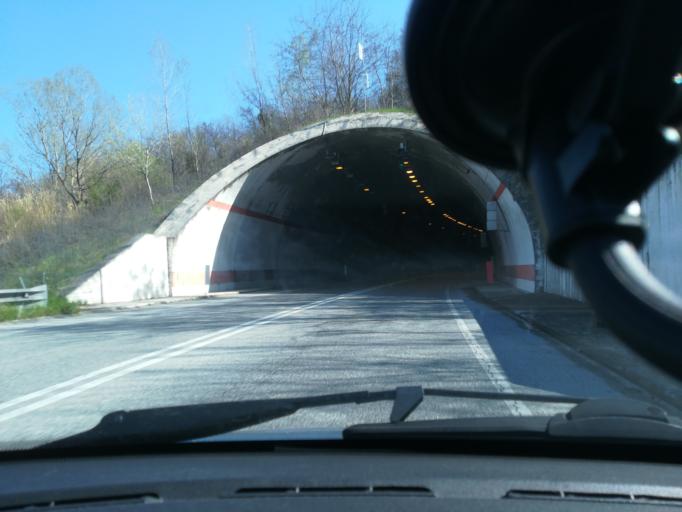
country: IT
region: The Marches
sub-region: Provincia di Macerata
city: Macerata
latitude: 43.3045
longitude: 13.4428
